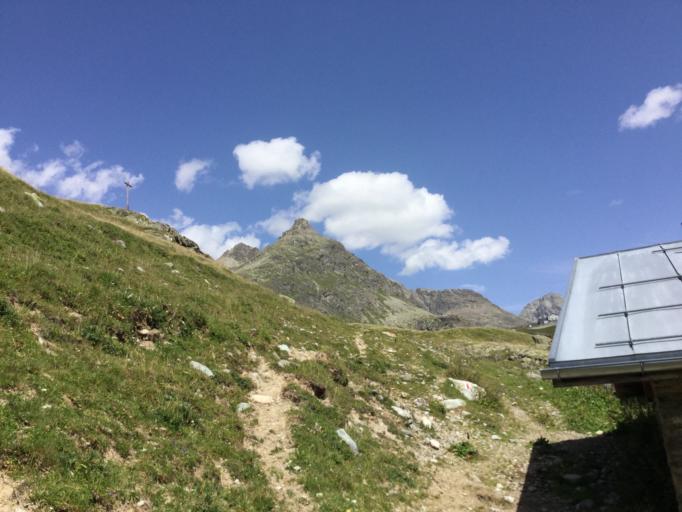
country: CH
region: Grisons
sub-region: Maloja District
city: Silvaplana
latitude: 46.4685
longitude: 9.7100
